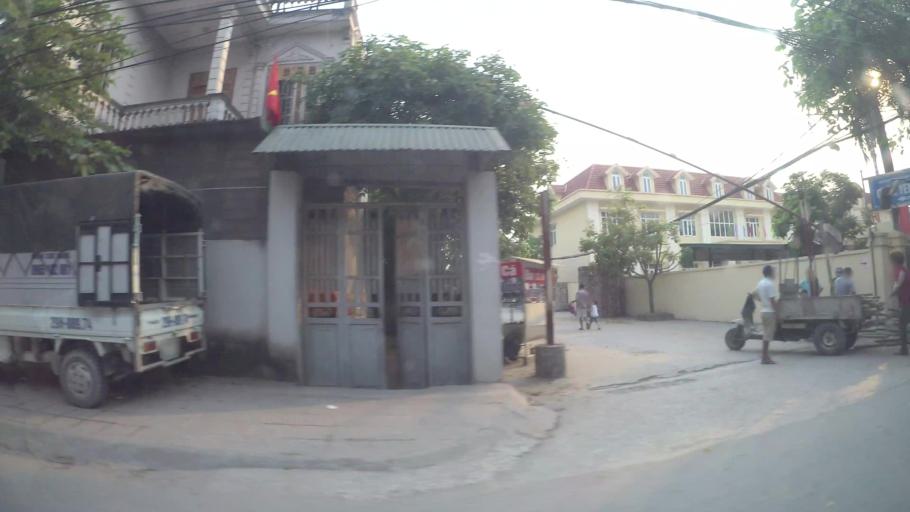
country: VN
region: Ha Noi
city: Van Dien
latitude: 20.9233
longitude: 105.8430
